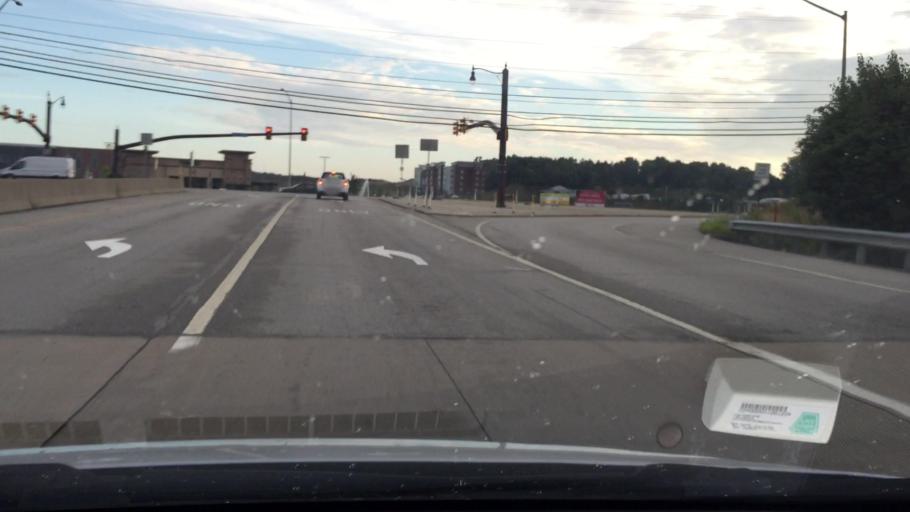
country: US
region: Pennsylvania
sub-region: Butler County
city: Cranberry Township
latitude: 40.6848
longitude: -80.0925
